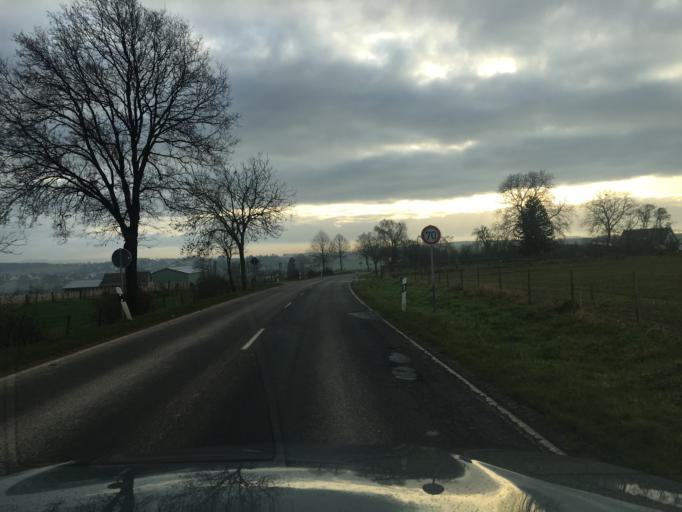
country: DE
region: North Rhine-Westphalia
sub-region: Regierungsbezirk Koln
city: Wachtberg
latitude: 50.6122
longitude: 7.1399
